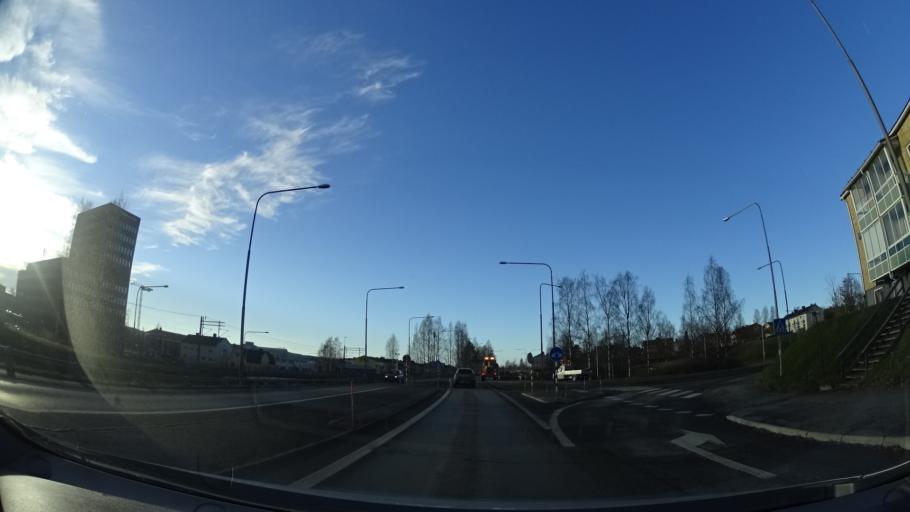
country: SE
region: Vaesterbotten
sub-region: Skelleftea Kommun
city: Skelleftea
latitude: 64.7533
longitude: 20.9639
